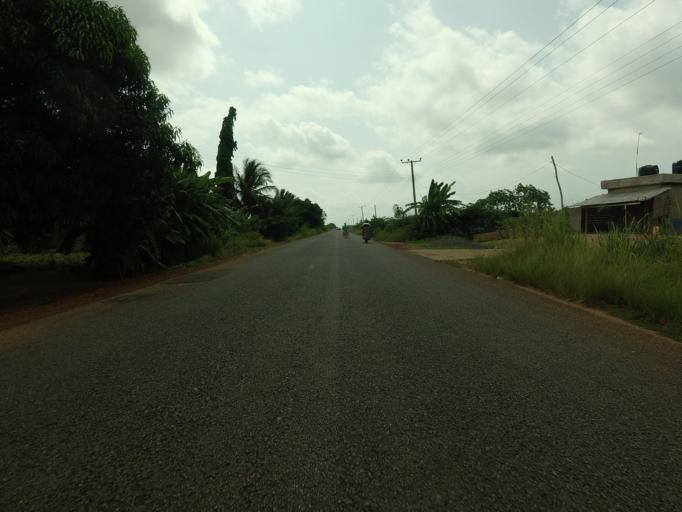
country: TG
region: Maritime
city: Lome
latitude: 6.1775
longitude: 1.0698
